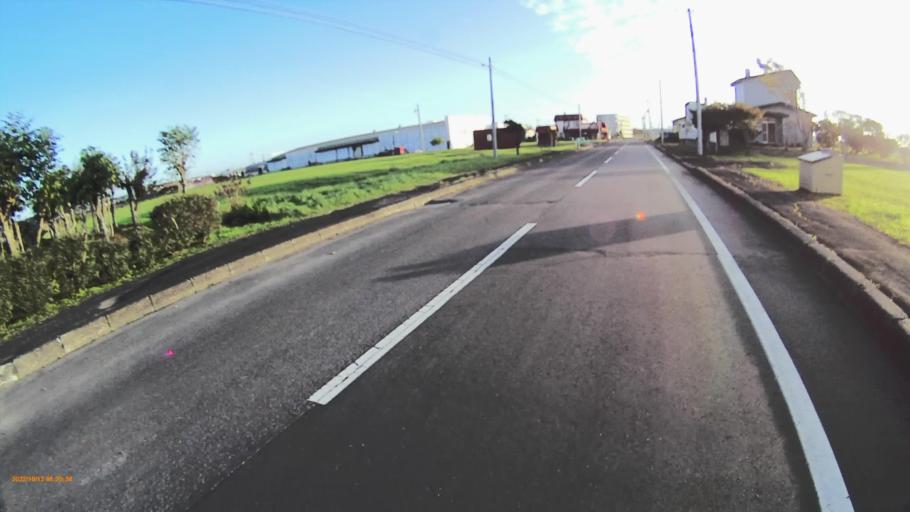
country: JP
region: Hokkaido
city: Kushiro
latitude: 42.8864
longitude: 143.9320
